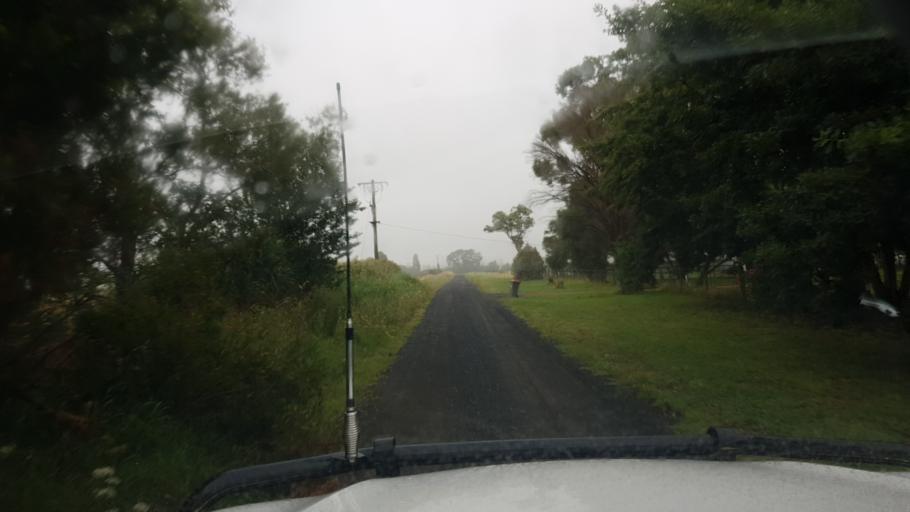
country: AU
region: Victoria
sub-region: Latrobe
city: Moe
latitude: -38.1990
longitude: 146.1729
